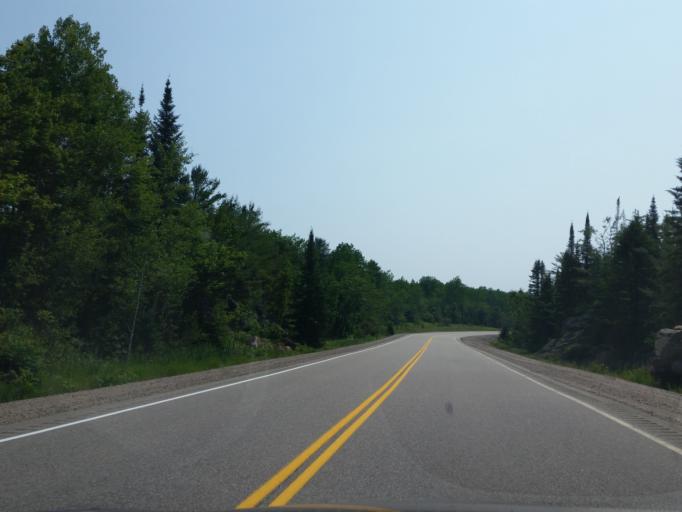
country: CA
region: Ontario
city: Mattawa
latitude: 46.2821
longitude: -78.3890
